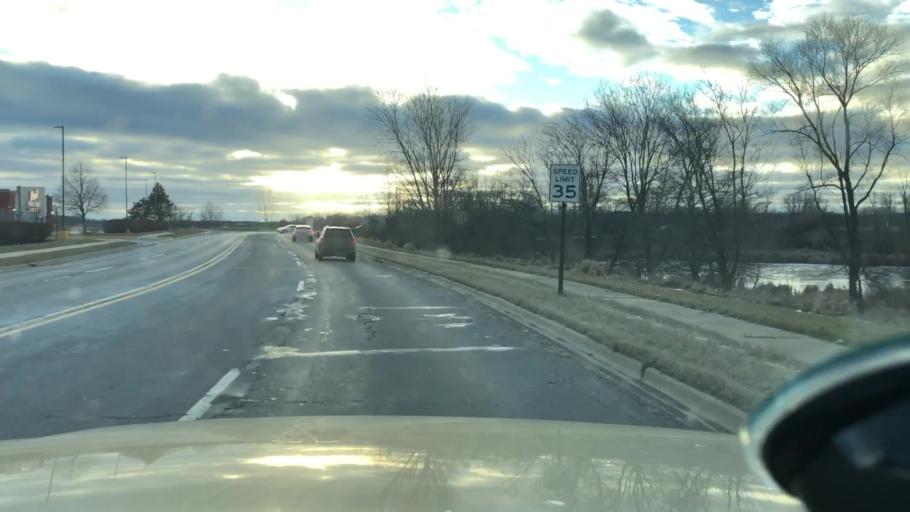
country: US
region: Michigan
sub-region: Jackson County
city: Jackson
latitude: 42.2663
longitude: -84.4583
